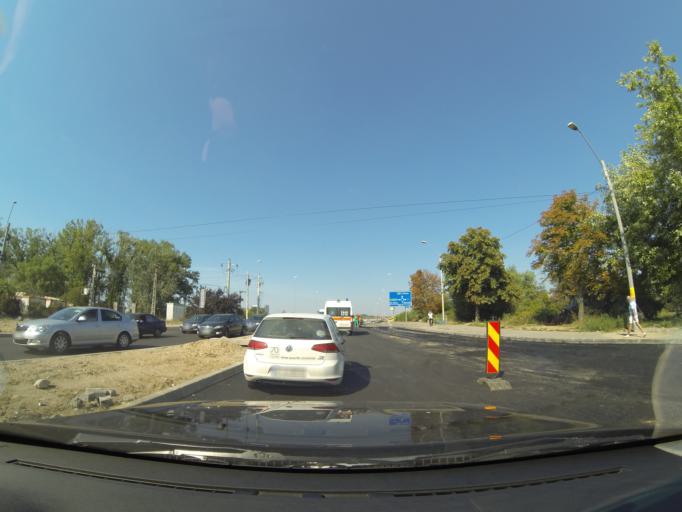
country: RO
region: Arges
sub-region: Comuna Albestii de Arges
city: Pitesti
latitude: 44.8652
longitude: 24.8801
